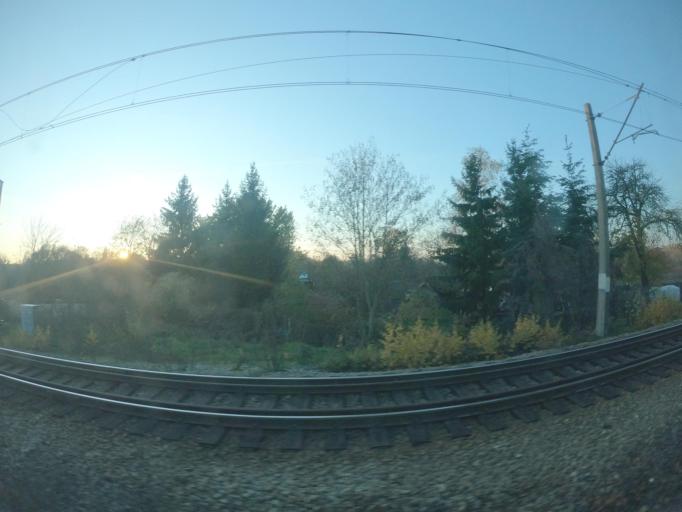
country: PL
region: Lubusz
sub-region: Powiat gorzowski
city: Kostrzyn nad Odra
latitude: 52.5830
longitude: 14.6428
